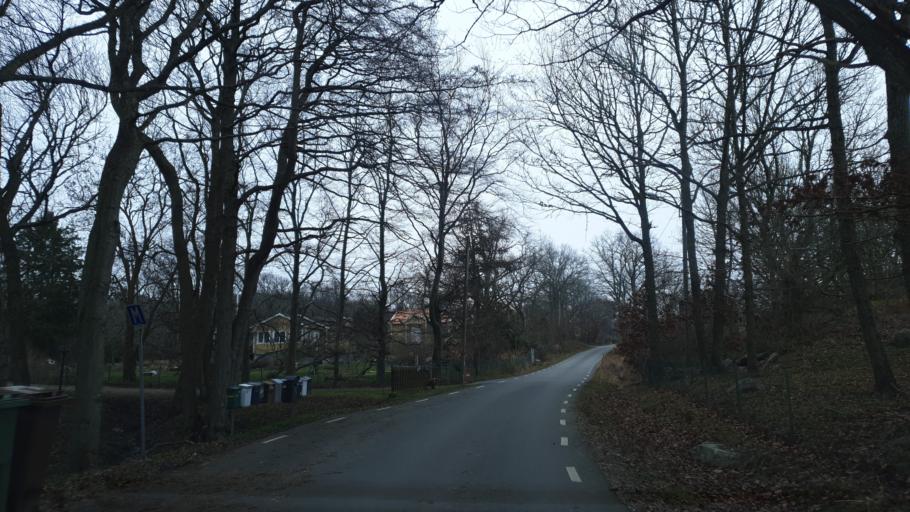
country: SE
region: Blekinge
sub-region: Karlskrona Kommun
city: Karlskrona
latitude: 56.1302
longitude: 15.6198
